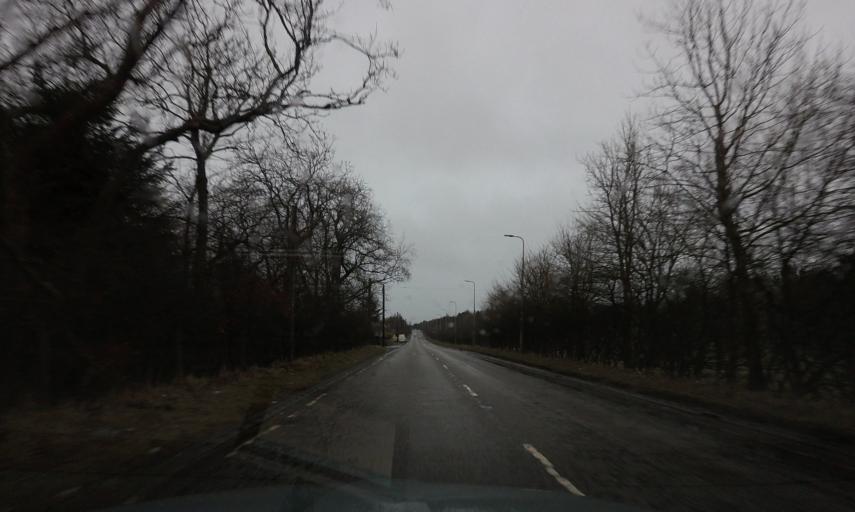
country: GB
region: Scotland
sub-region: North Lanarkshire
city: Shotts
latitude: 55.8540
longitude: -3.7978
